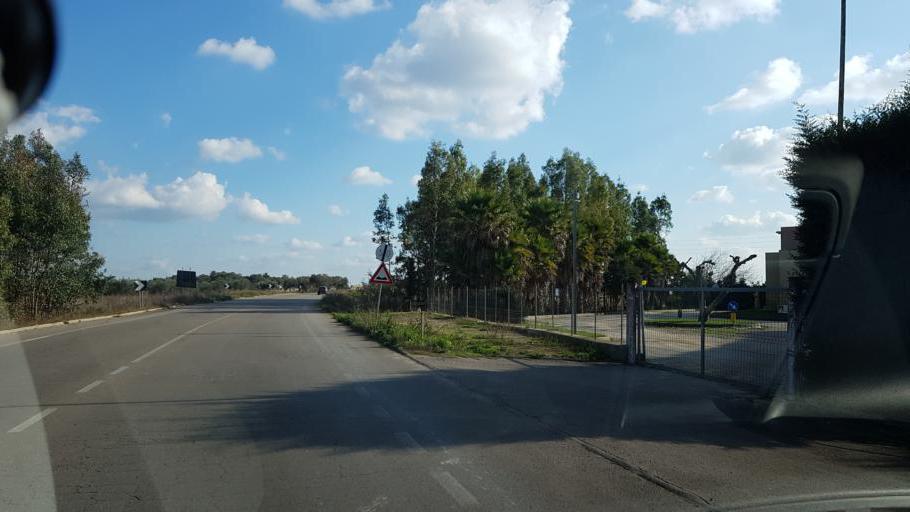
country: IT
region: Apulia
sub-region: Provincia di Lecce
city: Veglie
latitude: 40.3488
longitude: 17.9710
